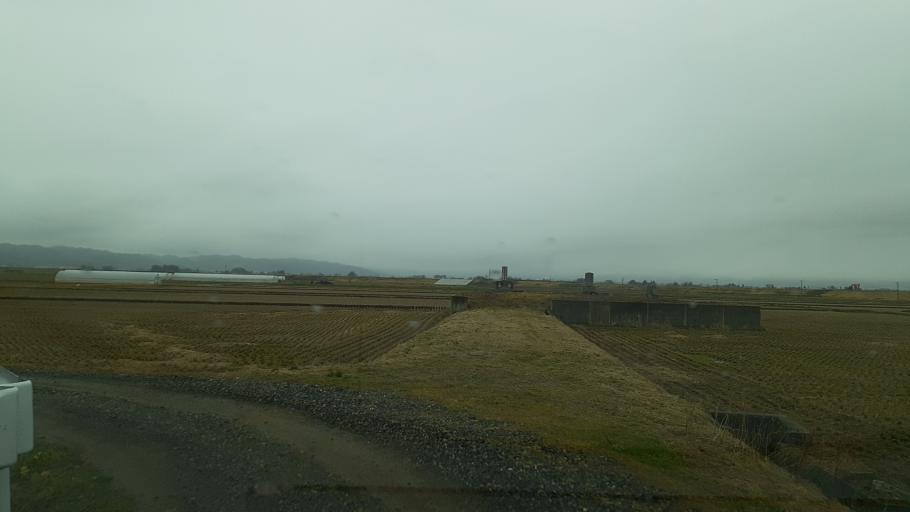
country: JP
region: Fukushima
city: Kitakata
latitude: 37.5854
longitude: 139.8563
